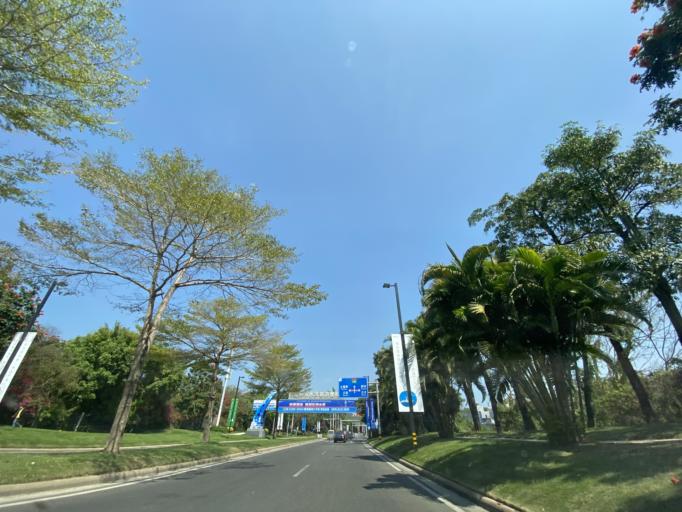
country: CN
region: Hainan
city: Yingzhou
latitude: 18.4219
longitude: 109.8450
